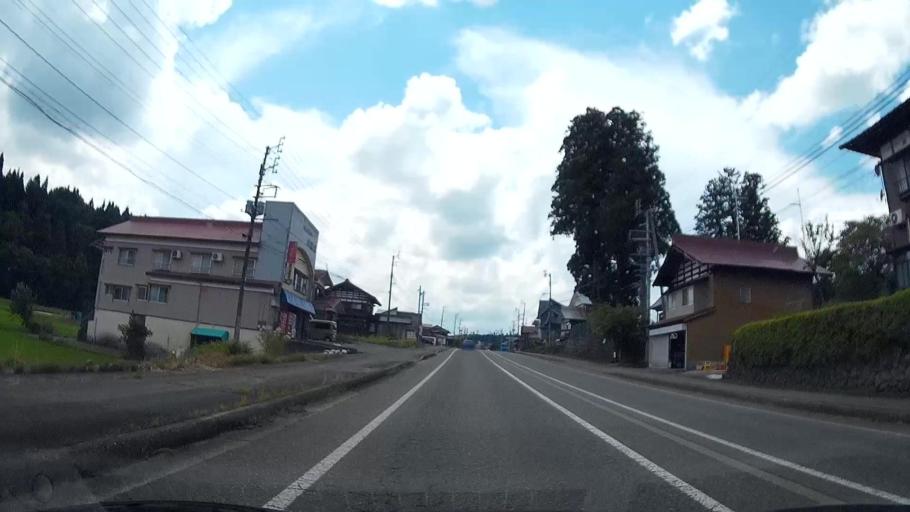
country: JP
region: Niigata
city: Tokamachi
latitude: 37.0410
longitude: 138.6789
